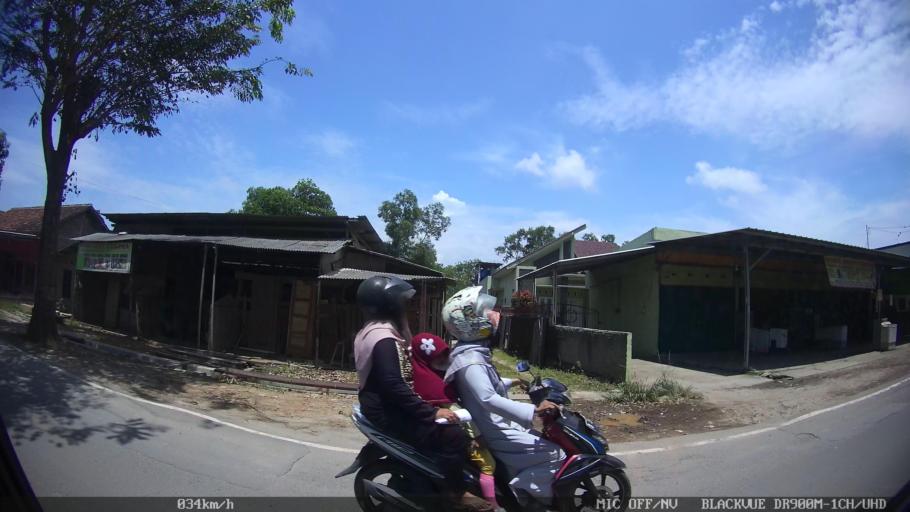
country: ID
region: Lampung
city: Kedaton
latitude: -5.3680
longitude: 105.2898
